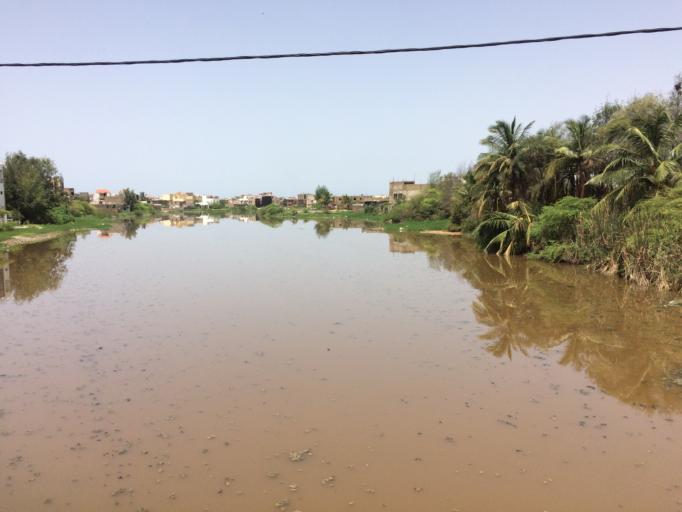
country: SN
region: Dakar
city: Pikine
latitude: 14.7335
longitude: -17.3264
